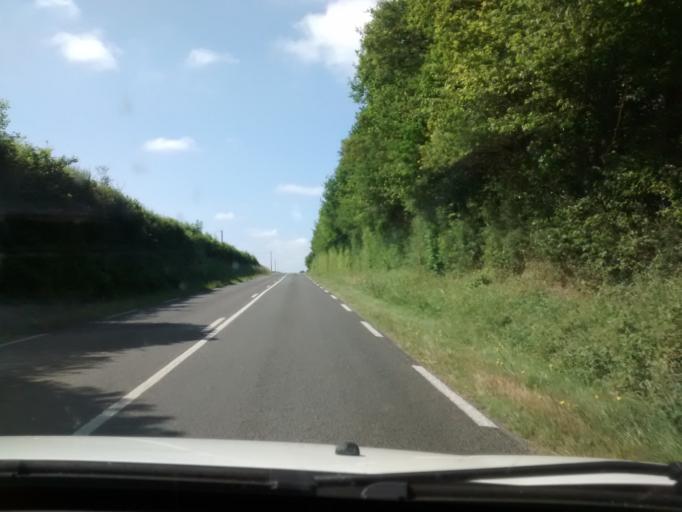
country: FR
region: Pays de la Loire
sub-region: Departement de la Sarthe
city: Saint-Calais
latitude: 47.9652
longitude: 0.7573
